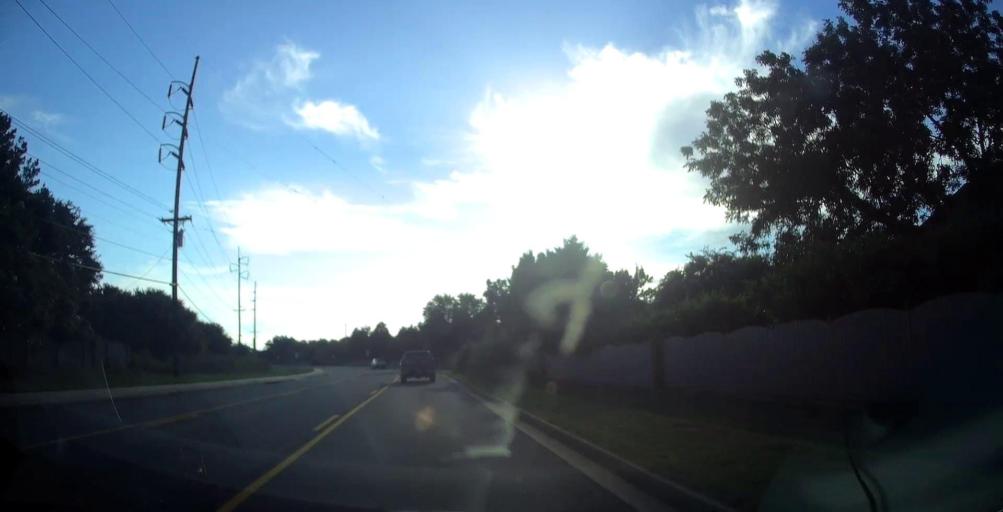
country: US
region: Georgia
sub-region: Houston County
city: Centerville
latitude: 32.6242
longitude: -83.6989
